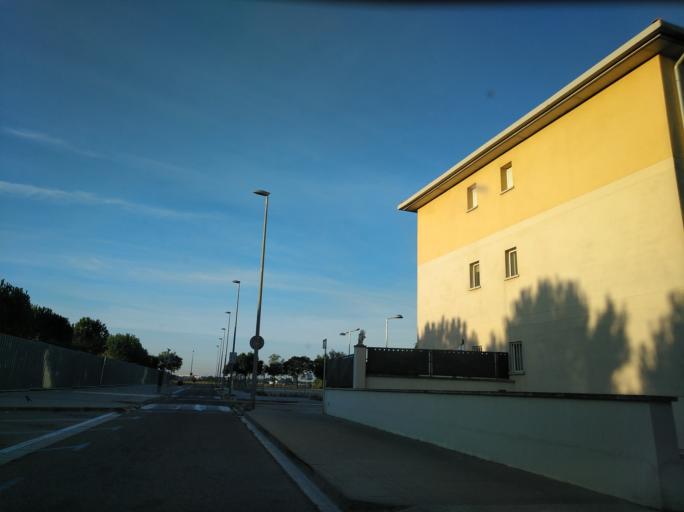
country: ES
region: Catalonia
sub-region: Provincia de Girona
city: Salt
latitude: 41.9699
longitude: 2.7945
